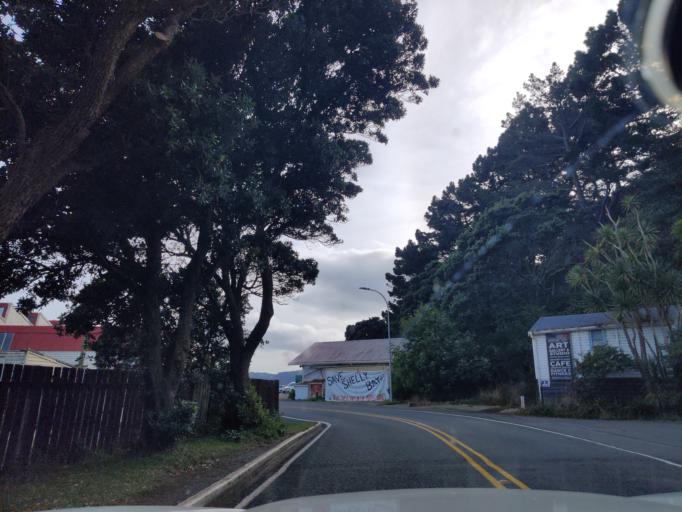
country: NZ
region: Wellington
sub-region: Wellington City
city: Wellington
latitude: -41.2948
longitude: 174.8221
